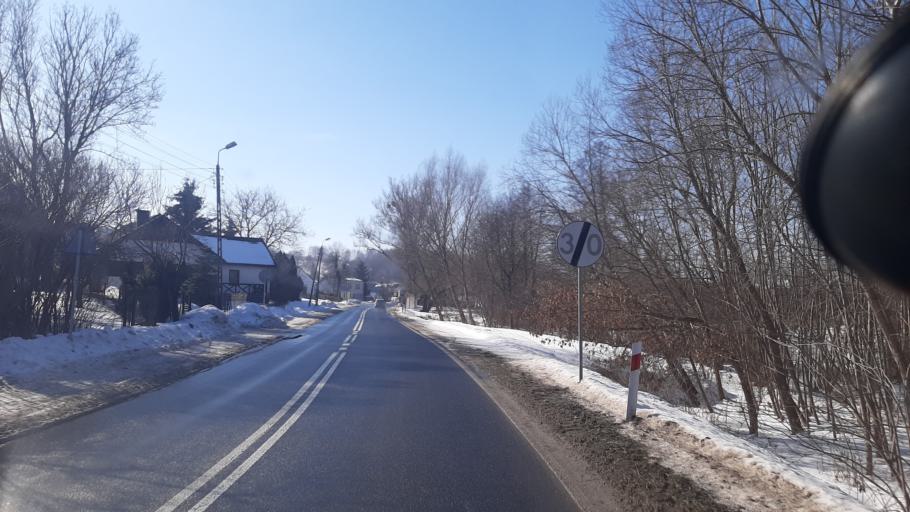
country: PL
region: Lublin Voivodeship
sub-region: Powiat pulawski
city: Naleczow
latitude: 51.2874
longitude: 22.1979
